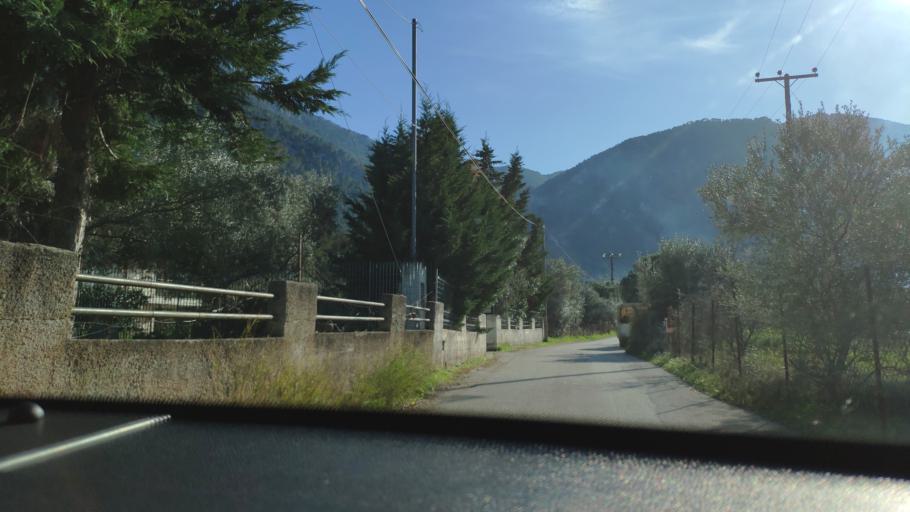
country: GR
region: Peloponnese
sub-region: Nomos Korinthias
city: Perachora
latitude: 38.0467
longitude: 23.0317
